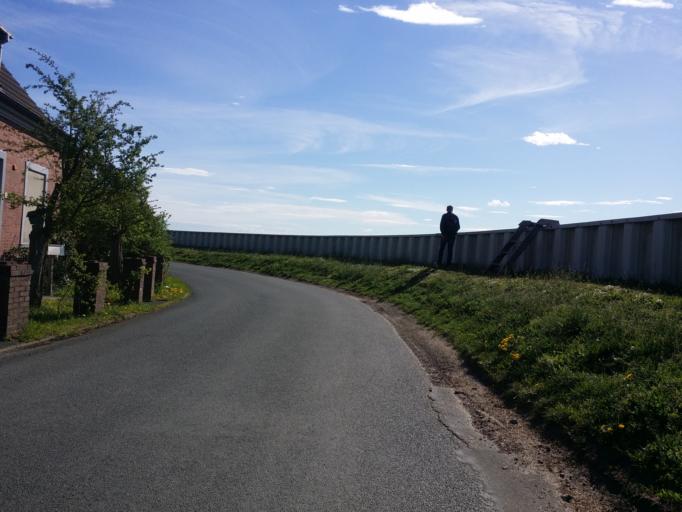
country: DE
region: Lower Saxony
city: Lemwerder
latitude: 53.1522
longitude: 8.6294
